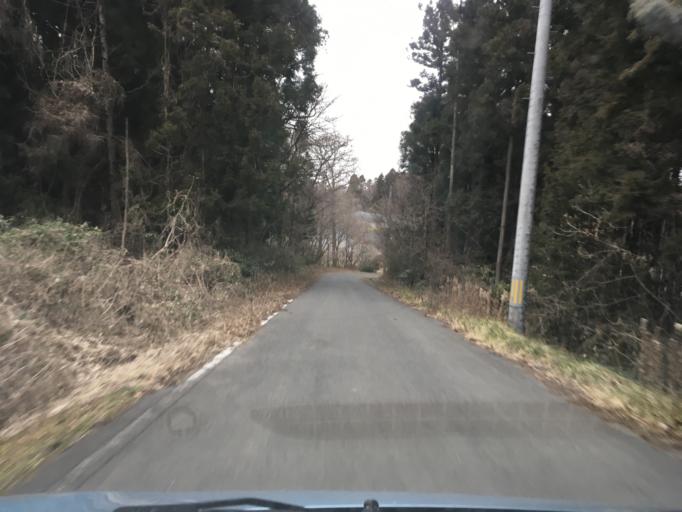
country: JP
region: Miyagi
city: Wakuya
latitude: 38.6634
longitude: 141.2816
